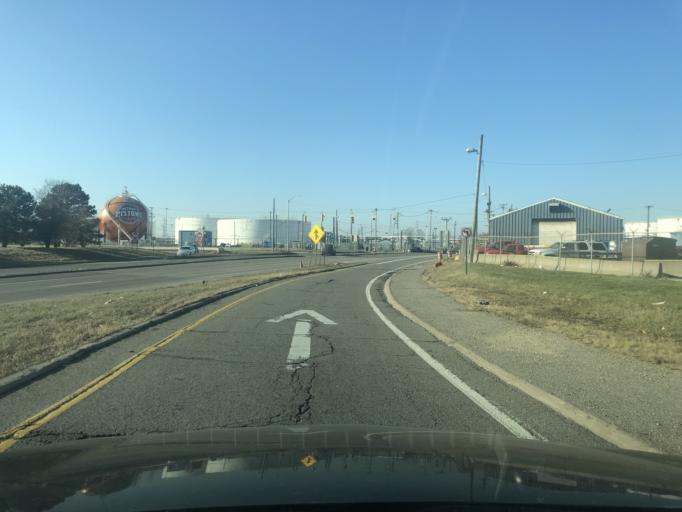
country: US
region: Michigan
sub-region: Wayne County
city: Melvindale
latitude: 42.2778
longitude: -83.1564
